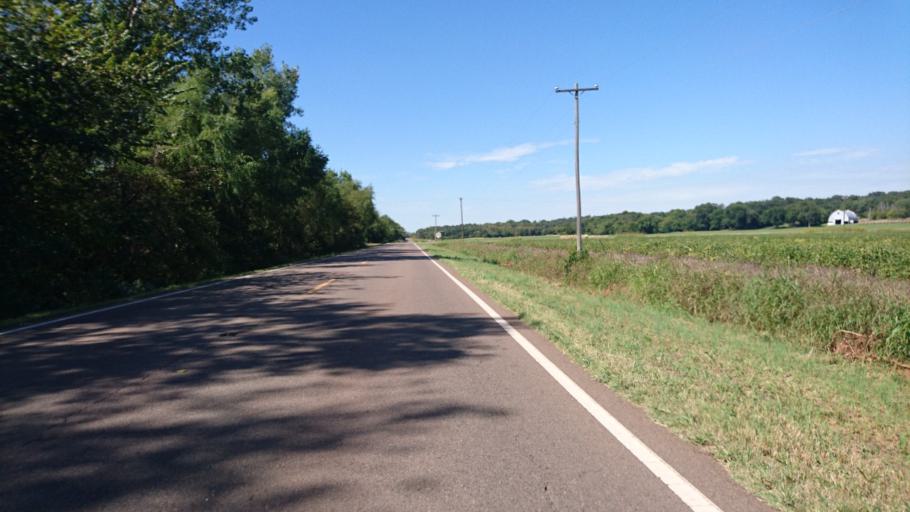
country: US
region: Oklahoma
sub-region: Oklahoma County
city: Luther
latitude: 35.6613
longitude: -97.2632
